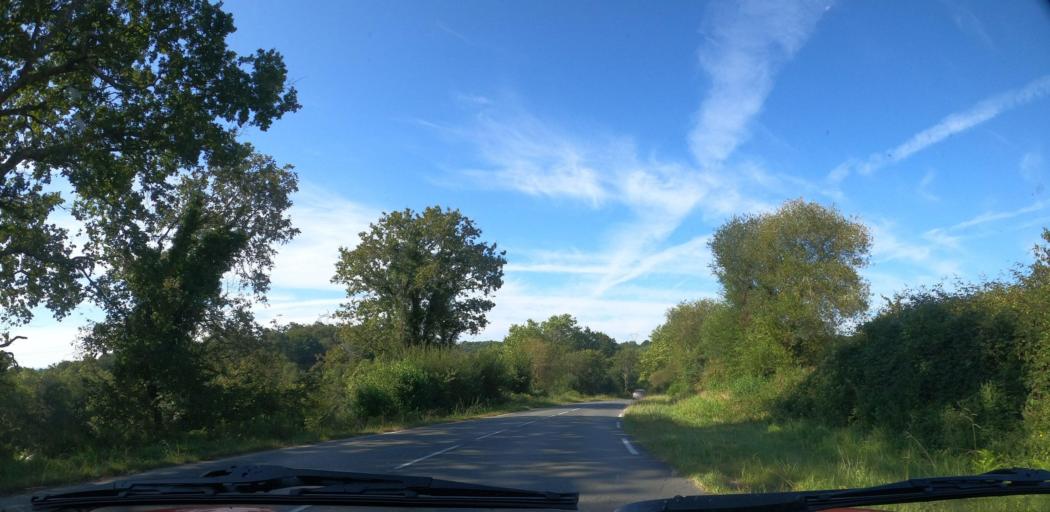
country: FR
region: Aquitaine
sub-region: Departement des Pyrenees-Atlantiques
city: Saint-Pee-sur-Nivelle
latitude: 43.3896
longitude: -1.5358
